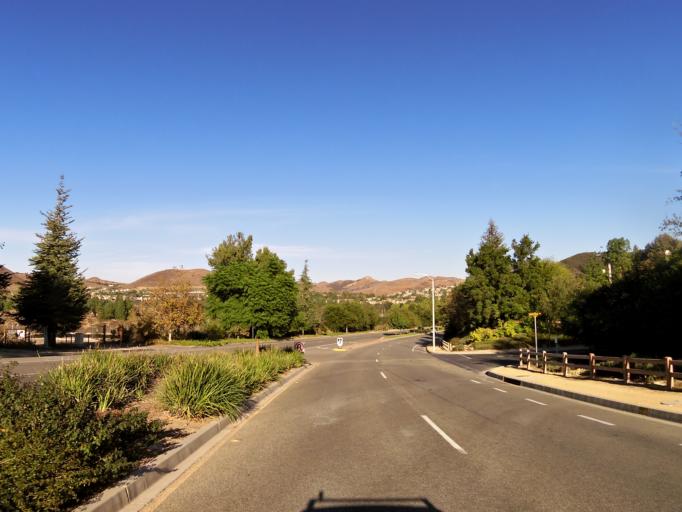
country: US
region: California
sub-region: Ventura County
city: Thousand Oaks
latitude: 34.2084
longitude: -118.8281
